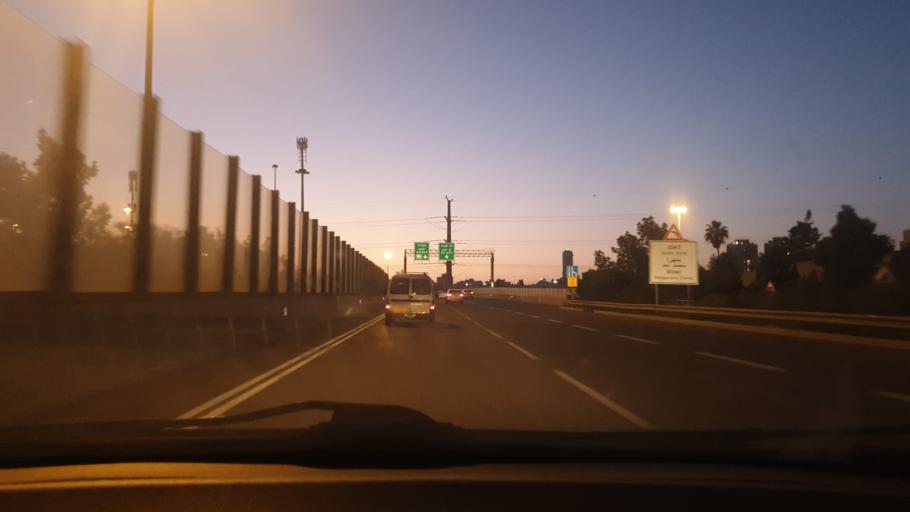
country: IL
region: Tel Aviv
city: Giv`at Shemu'el
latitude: 32.0650
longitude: 34.8408
